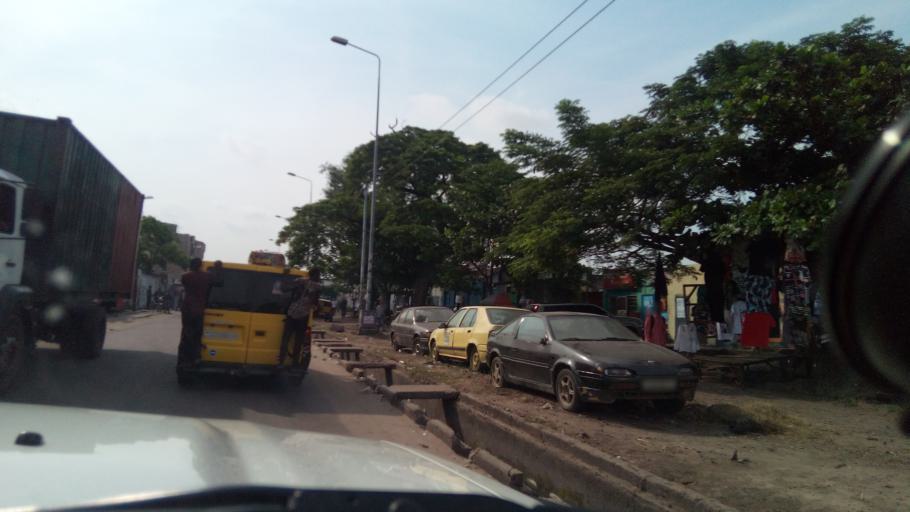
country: CD
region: Kinshasa
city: Kinshasa
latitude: -4.3488
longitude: 15.3182
